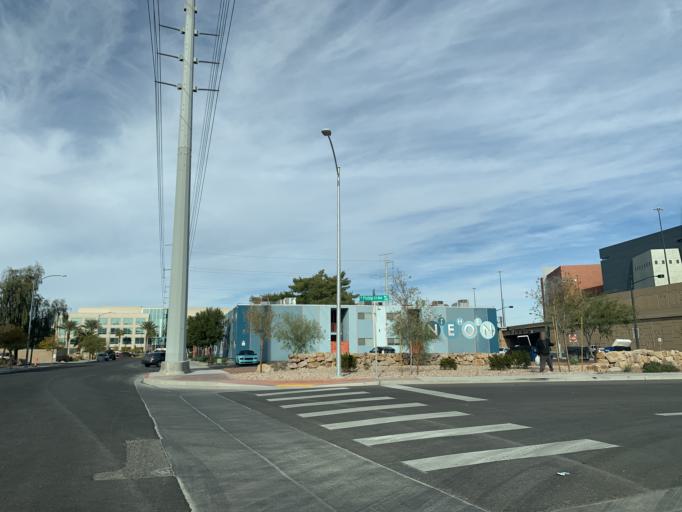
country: US
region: Nevada
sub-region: Clark County
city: Las Vegas
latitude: 36.1650
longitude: -115.1620
